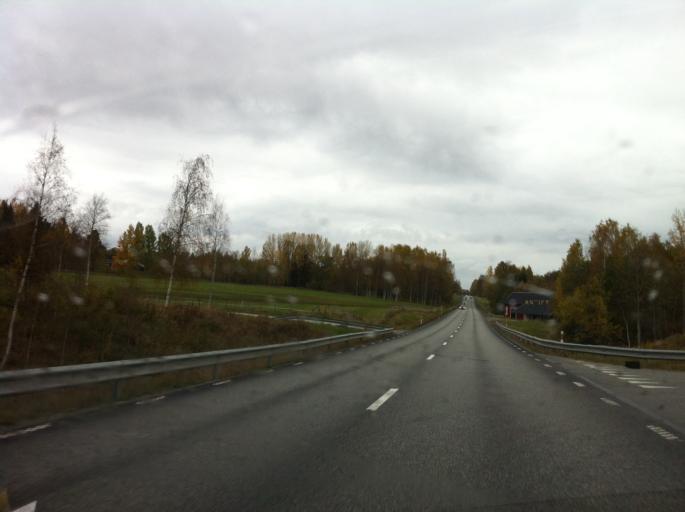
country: SE
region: OErebro
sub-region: Lindesbergs Kommun
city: Stora
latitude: 59.6780
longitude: 15.0996
